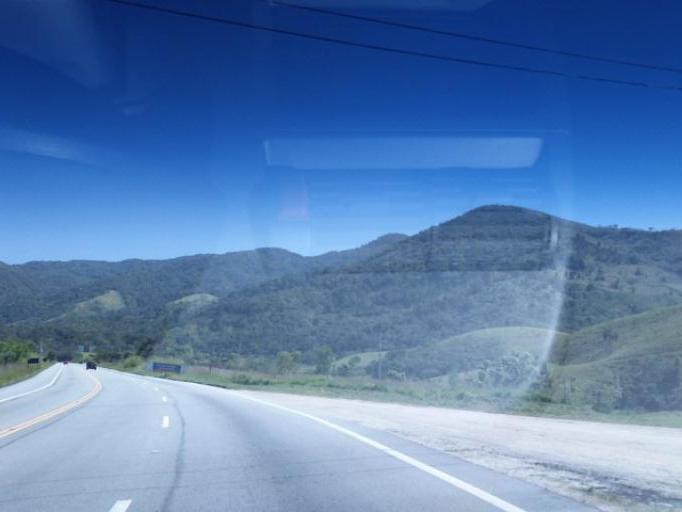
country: BR
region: Sao Paulo
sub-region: Tremembe
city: Tremembe
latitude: -22.8598
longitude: -45.6109
